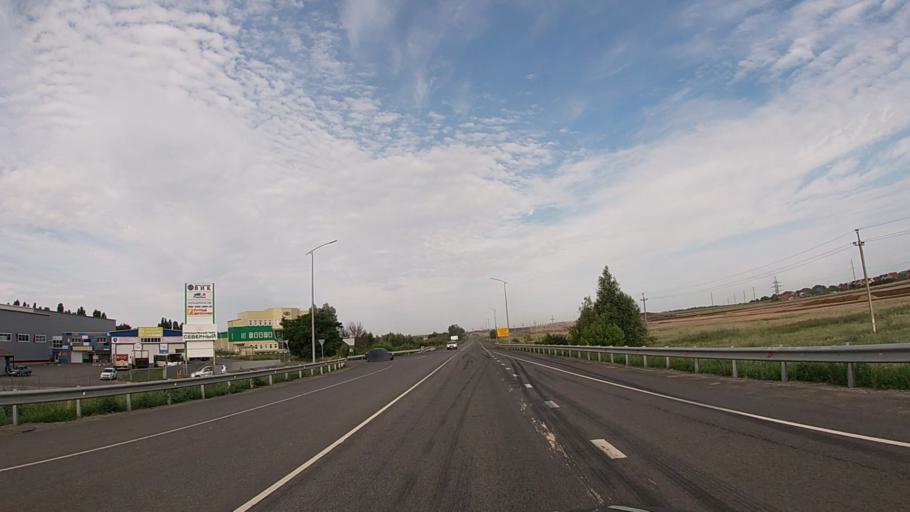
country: RU
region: Belgorod
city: Severnyy
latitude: 50.6675
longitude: 36.5535
